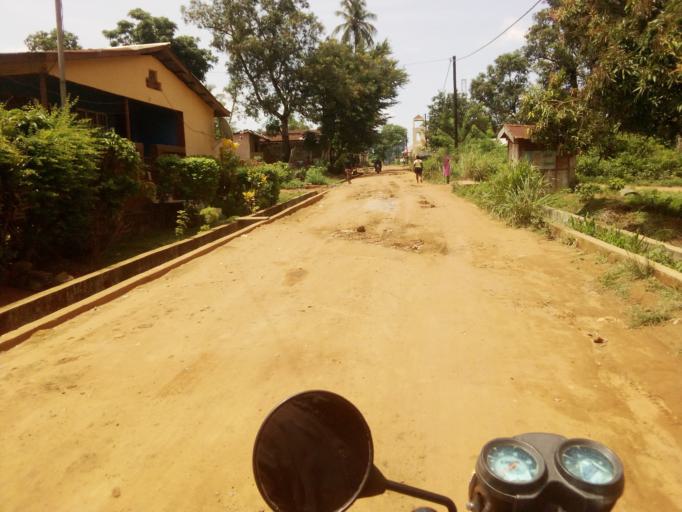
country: SL
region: Western Area
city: Waterloo
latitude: 8.3384
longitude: -13.0690
